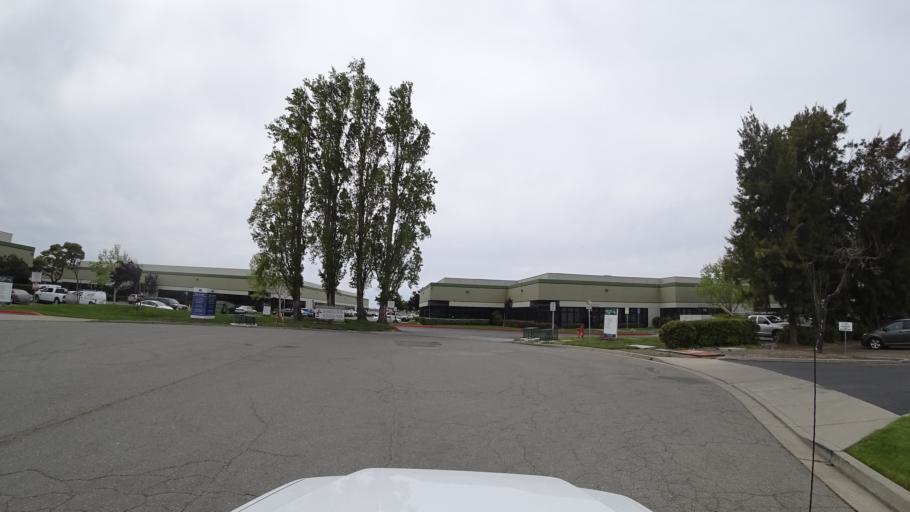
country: US
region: California
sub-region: Alameda County
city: San Lorenzo
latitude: 37.6553
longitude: -122.1422
